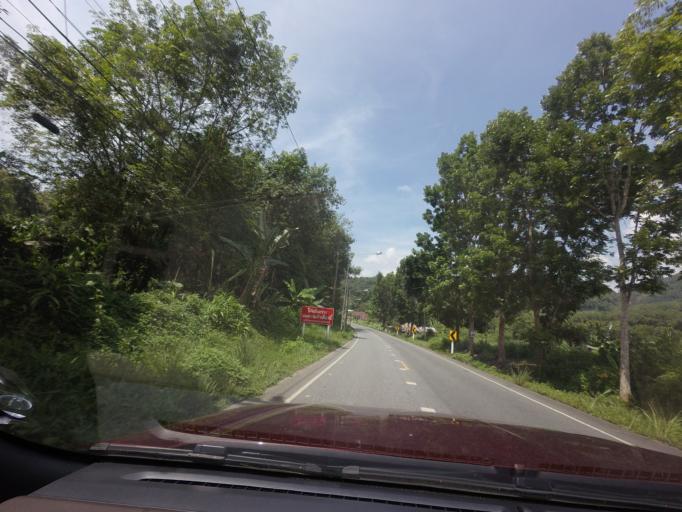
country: TH
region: Yala
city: Betong
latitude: 5.8397
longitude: 101.0741
